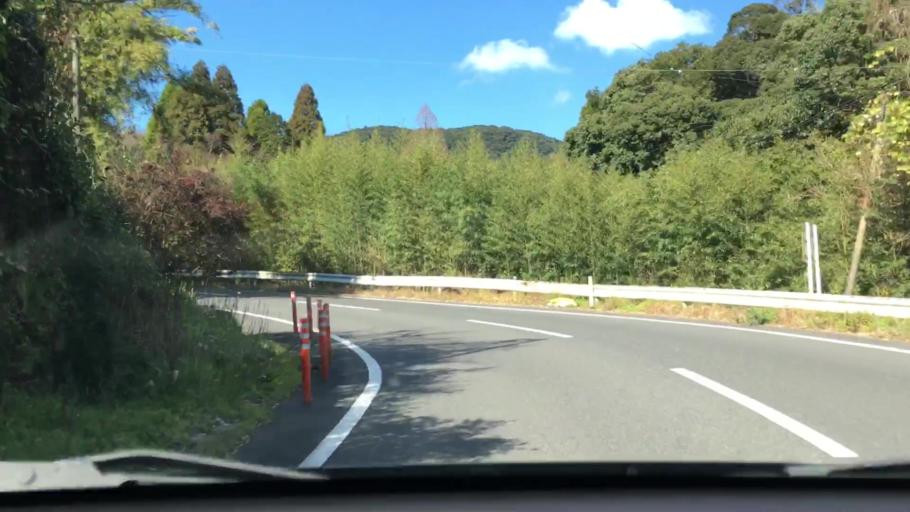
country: JP
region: Kagoshima
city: Ijuin
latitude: 31.7157
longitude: 130.4336
